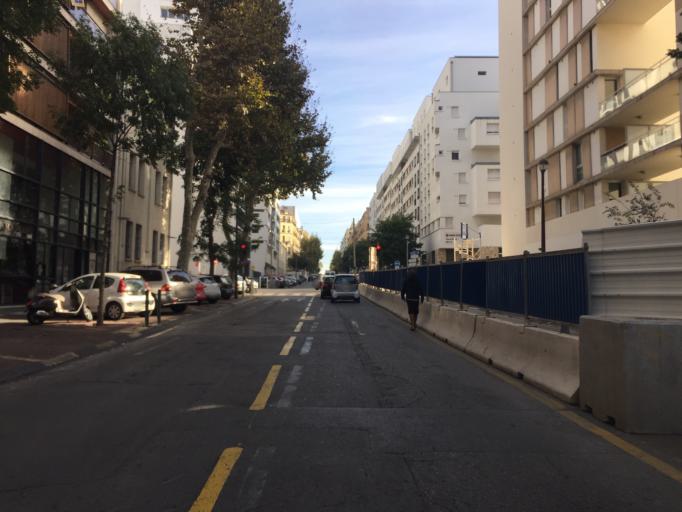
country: FR
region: Provence-Alpes-Cote d'Azur
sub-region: Departement des Bouches-du-Rhone
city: Marseille 03
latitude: 43.3104
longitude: 5.3699
